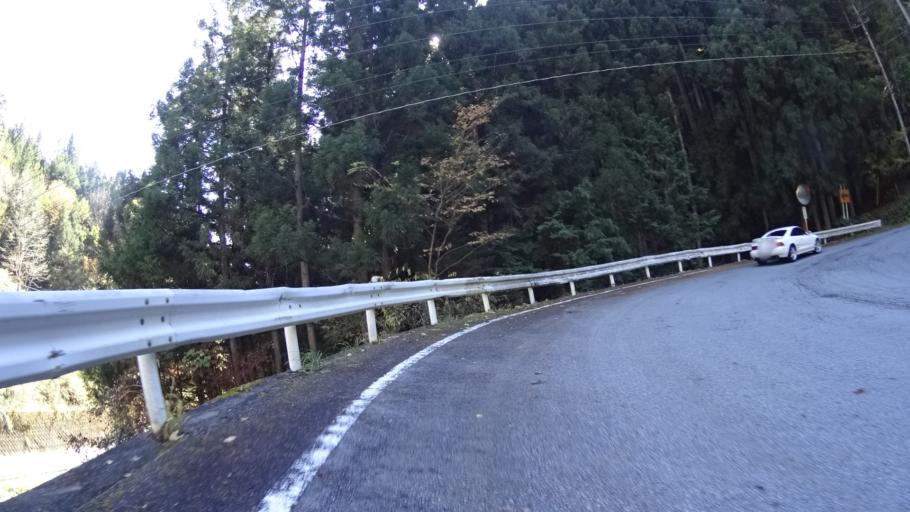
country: JP
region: Yamanashi
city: Otsuki
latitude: 35.7659
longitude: 138.9353
